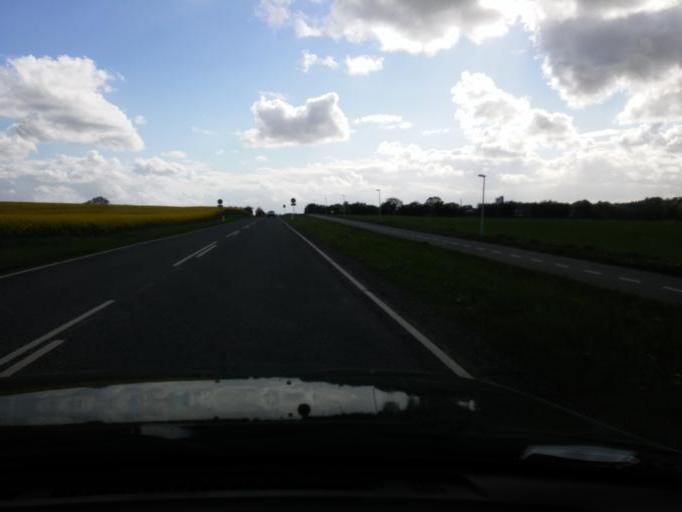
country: DK
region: South Denmark
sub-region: Faaborg-Midtfyn Kommune
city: Ringe
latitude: 55.2422
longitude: 10.5044
